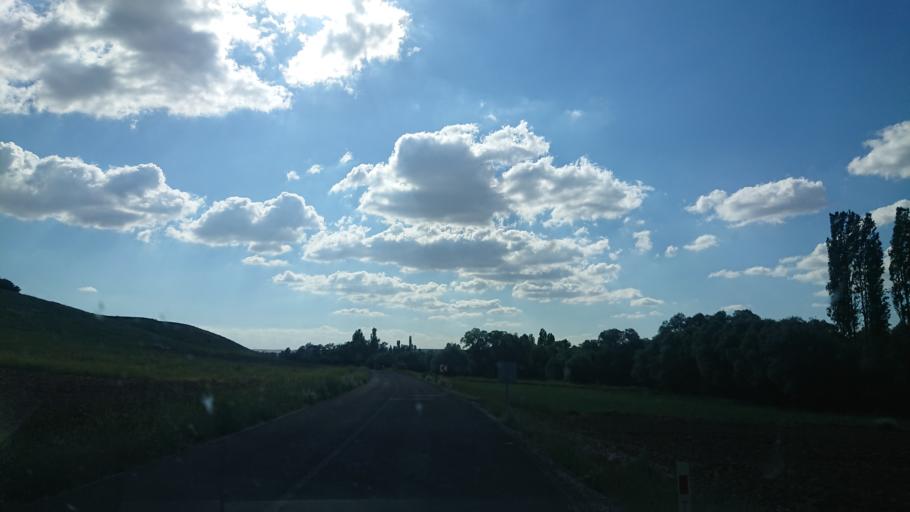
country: TR
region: Aksaray
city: Agacoren
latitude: 38.7579
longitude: 33.9100
